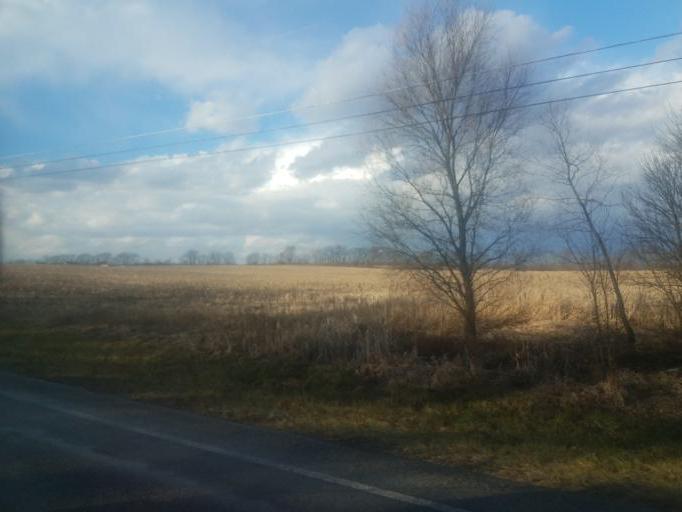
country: US
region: Ohio
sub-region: Delaware County
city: Delaware
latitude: 40.3366
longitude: -83.1254
